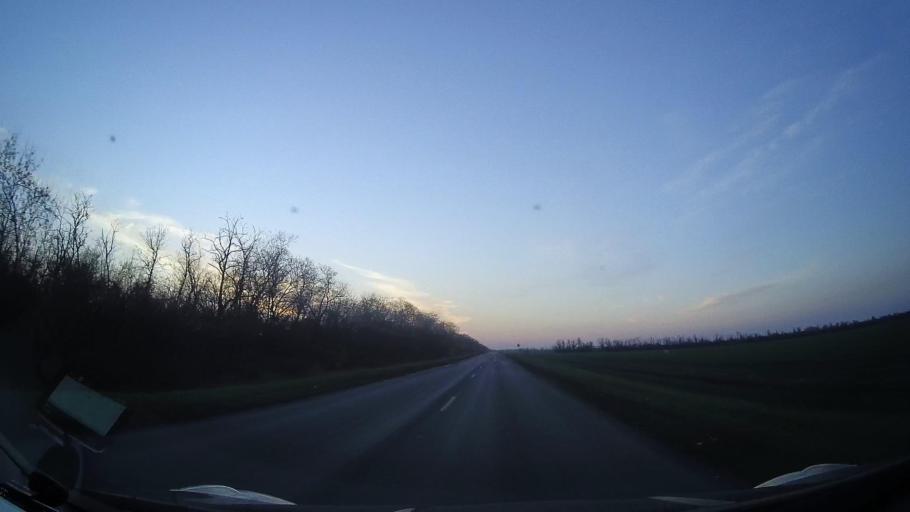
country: RU
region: Rostov
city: Zernograd
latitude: 46.9251
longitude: 40.3564
